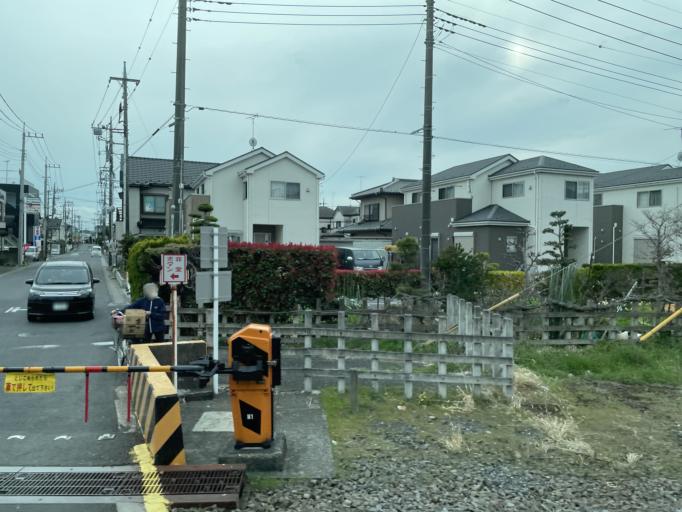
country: JP
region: Saitama
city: Sugito
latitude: 36.0215
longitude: 139.7318
